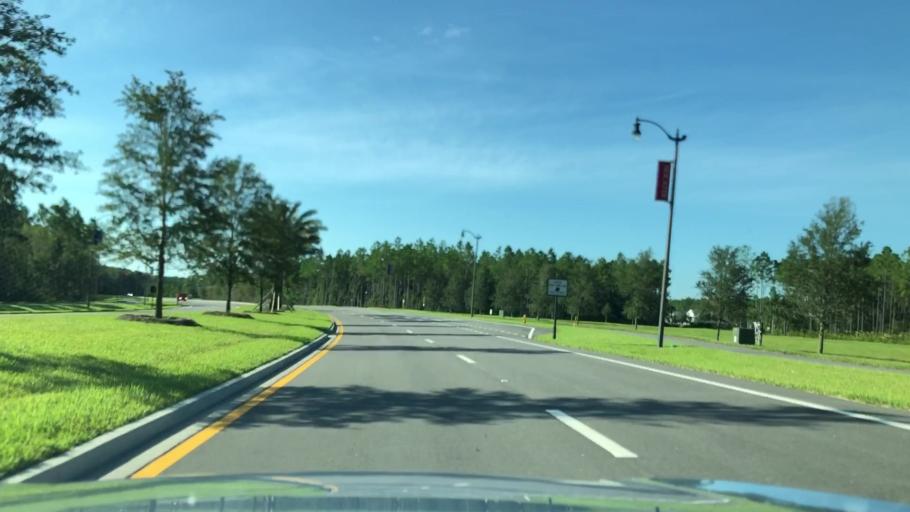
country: US
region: Florida
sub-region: Saint Johns County
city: Palm Valley
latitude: 30.0853
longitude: -81.4055
